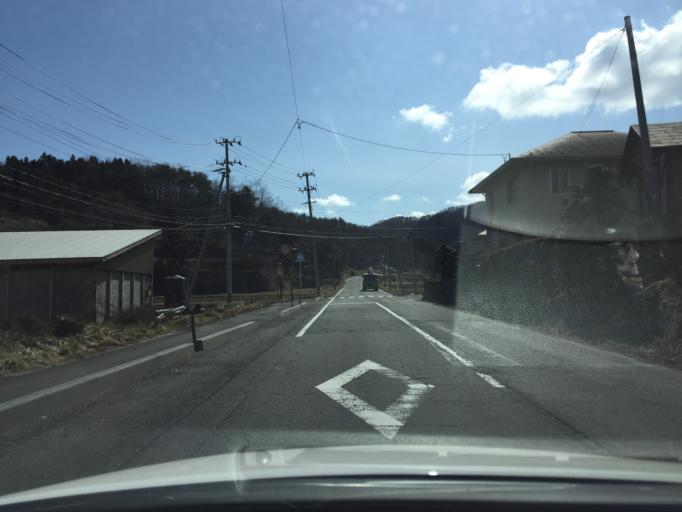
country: JP
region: Fukushima
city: Funehikimachi-funehiki
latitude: 37.3824
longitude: 140.5957
